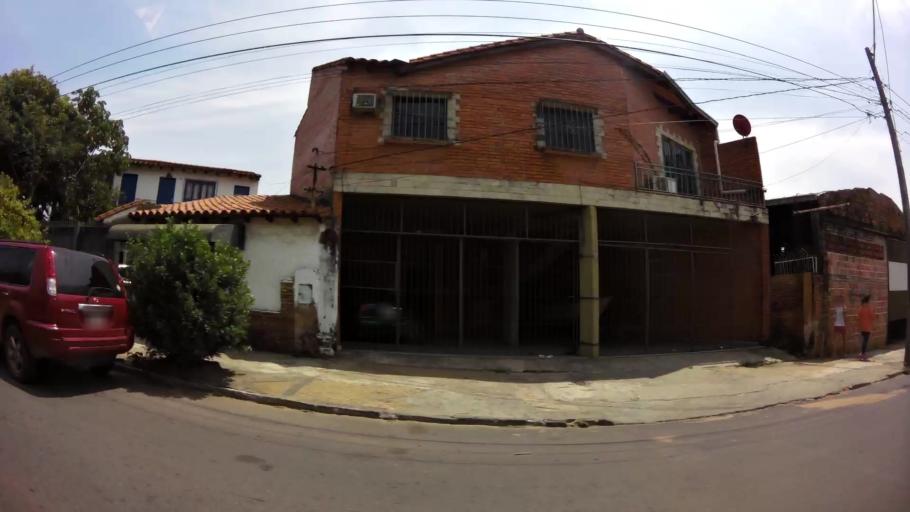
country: PY
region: Asuncion
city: Asuncion
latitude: -25.2712
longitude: -57.5982
